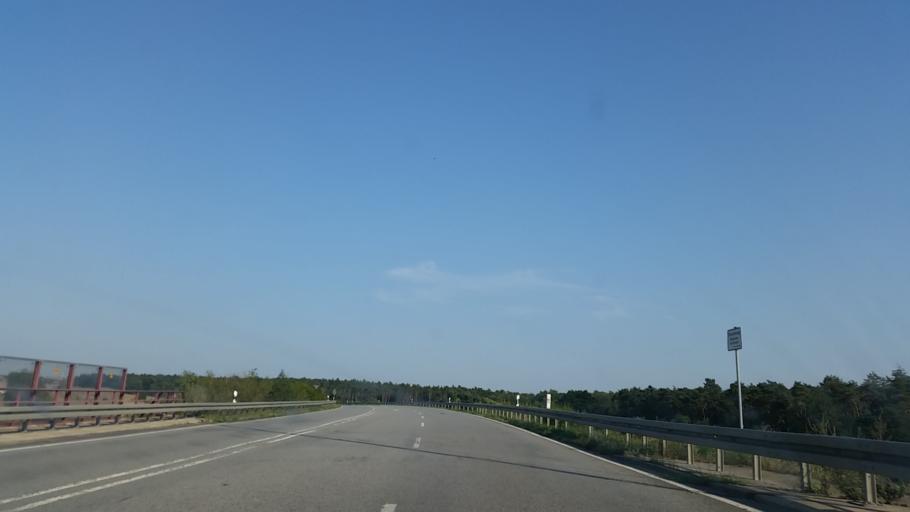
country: DE
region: Brandenburg
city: Pinnow
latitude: 53.0703
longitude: 14.1163
